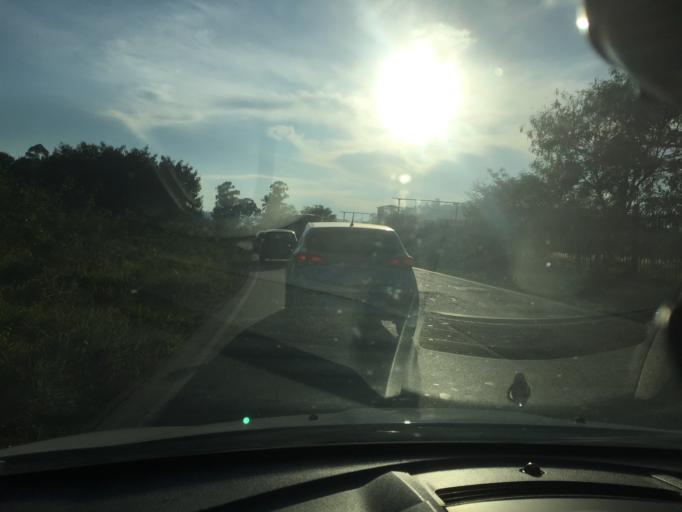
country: BR
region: Sao Paulo
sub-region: Varzea Paulista
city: Varzea Paulista
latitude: -23.2078
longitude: -46.8267
